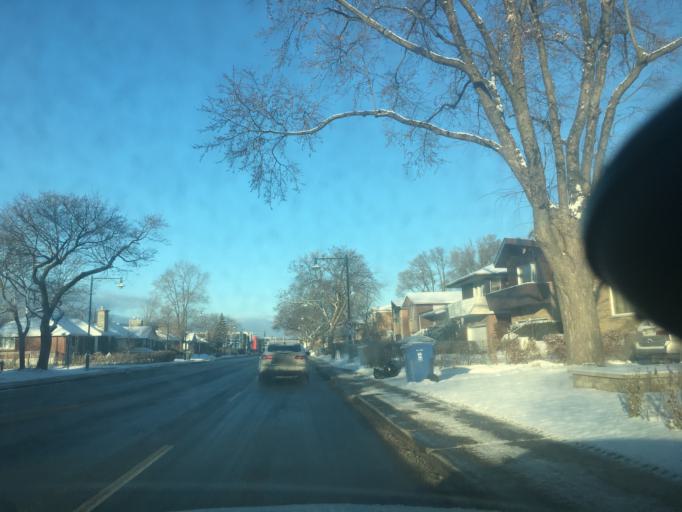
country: CA
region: Quebec
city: Saint-Laurent
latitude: 45.5064
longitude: -73.6577
